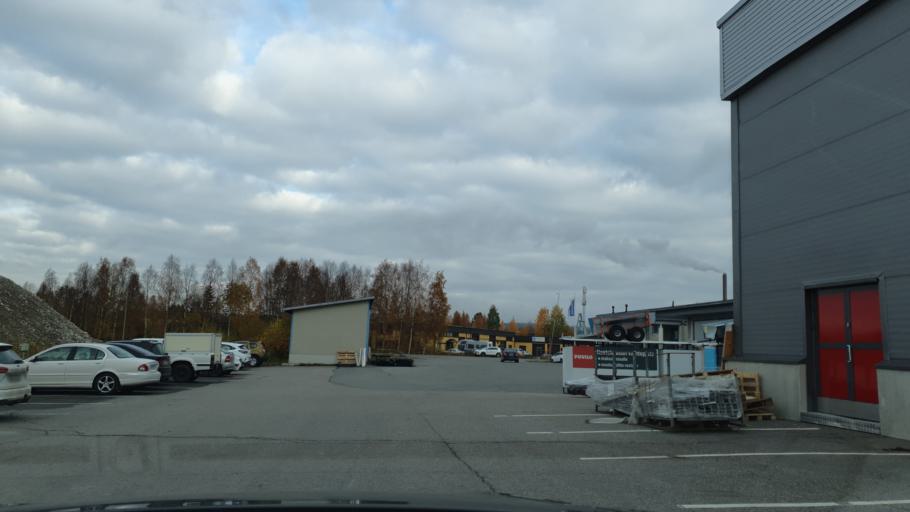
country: FI
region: Lapland
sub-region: Rovaniemi
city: Rovaniemi
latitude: 66.4899
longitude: 25.6695
